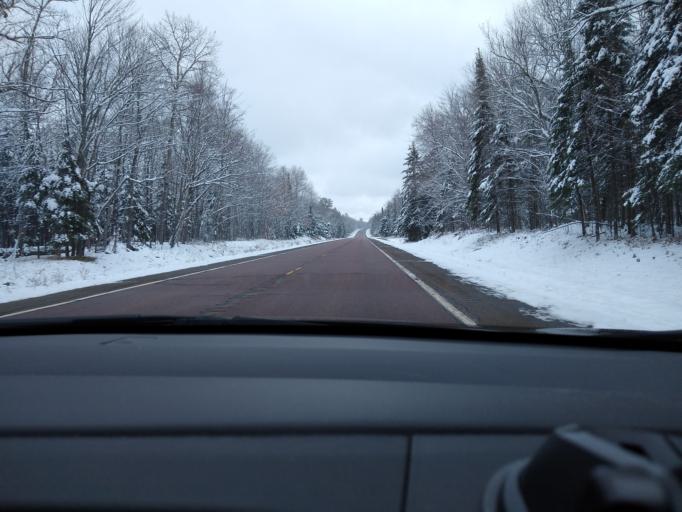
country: US
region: Michigan
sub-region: Iron County
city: Iron River
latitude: 46.1831
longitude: -88.9687
